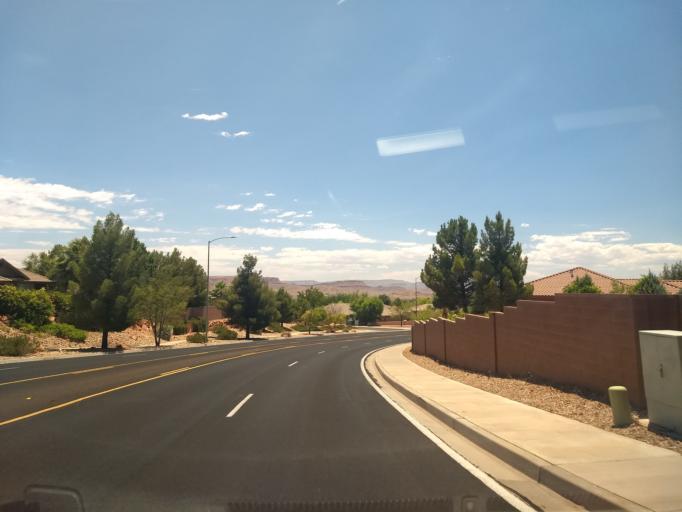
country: US
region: Utah
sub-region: Washington County
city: Washington
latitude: 37.1441
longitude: -113.5293
